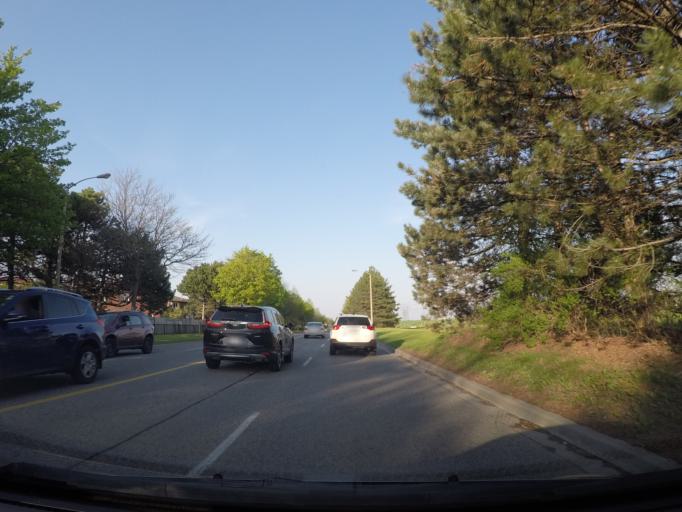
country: CA
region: Ontario
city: Scarborough
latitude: 43.8171
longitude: -79.2758
